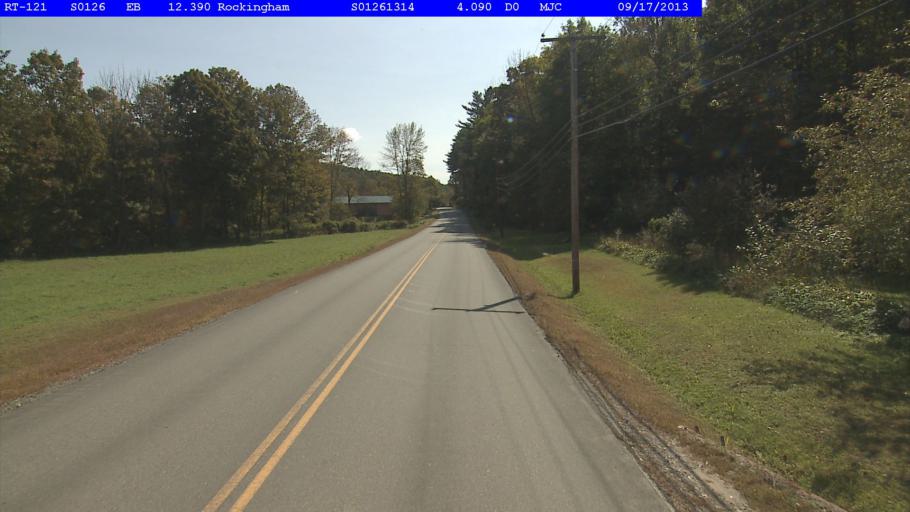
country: US
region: Vermont
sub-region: Windham County
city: Bellows Falls
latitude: 43.1383
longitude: -72.4897
